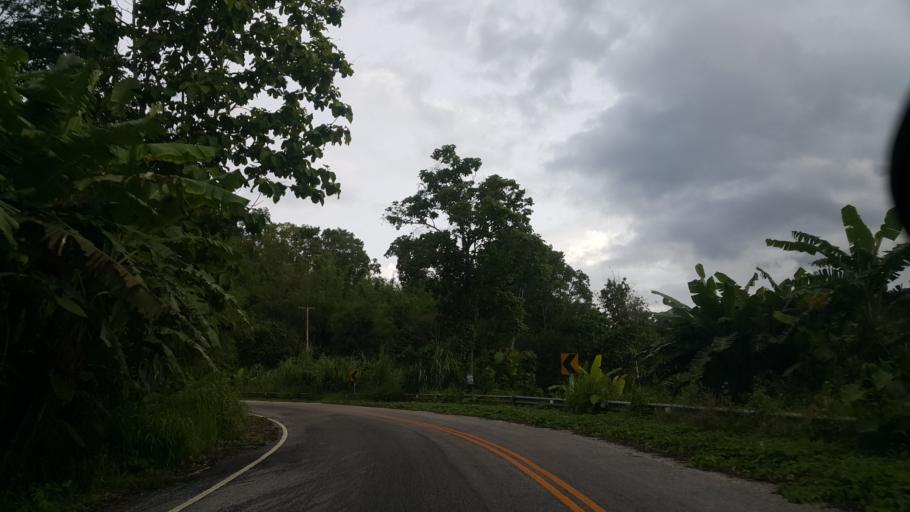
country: TH
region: Loei
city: Na Haeo
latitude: 17.4769
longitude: 101.1133
